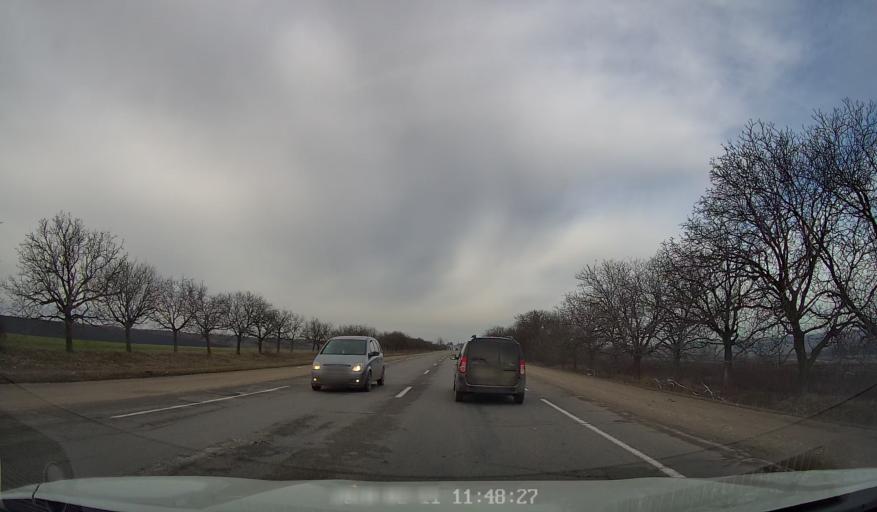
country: MD
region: Balti
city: Balti
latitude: 47.8386
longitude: 27.8031
